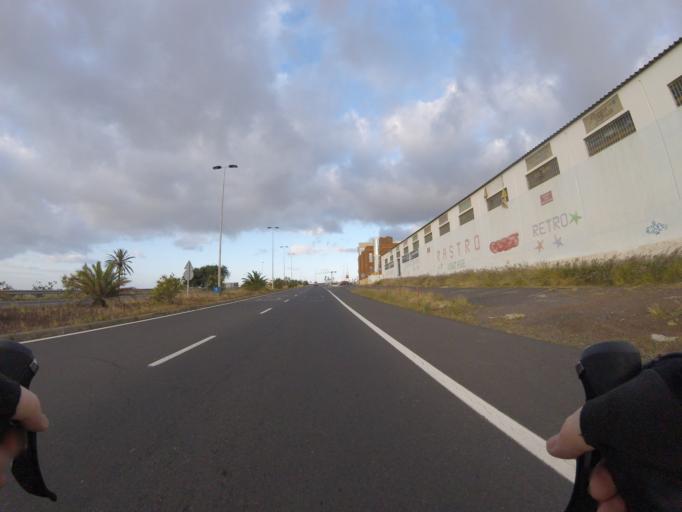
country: ES
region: Canary Islands
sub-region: Provincia de Santa Cruz de Tenerife
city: La Laguna
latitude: 28.4292
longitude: -16.3124
